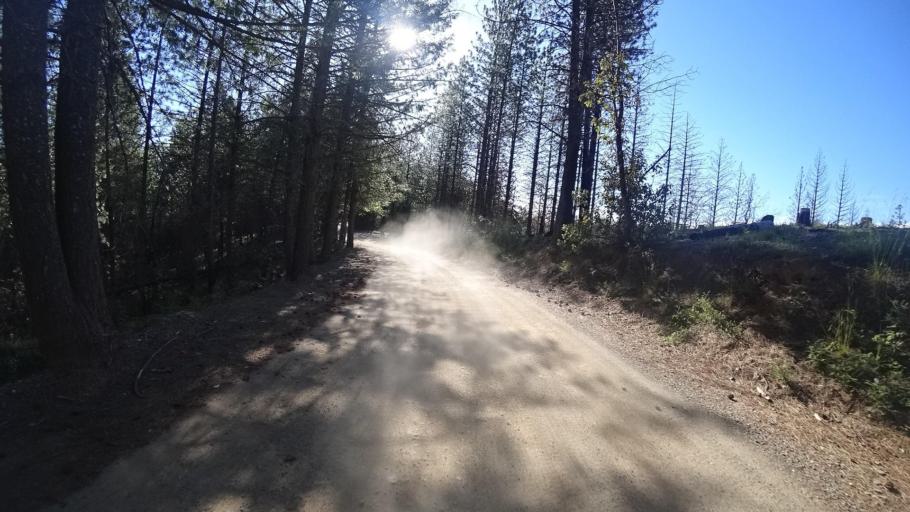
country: US
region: California
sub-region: Lake County
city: Upper Lake
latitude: 39.3497
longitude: -122.9735
